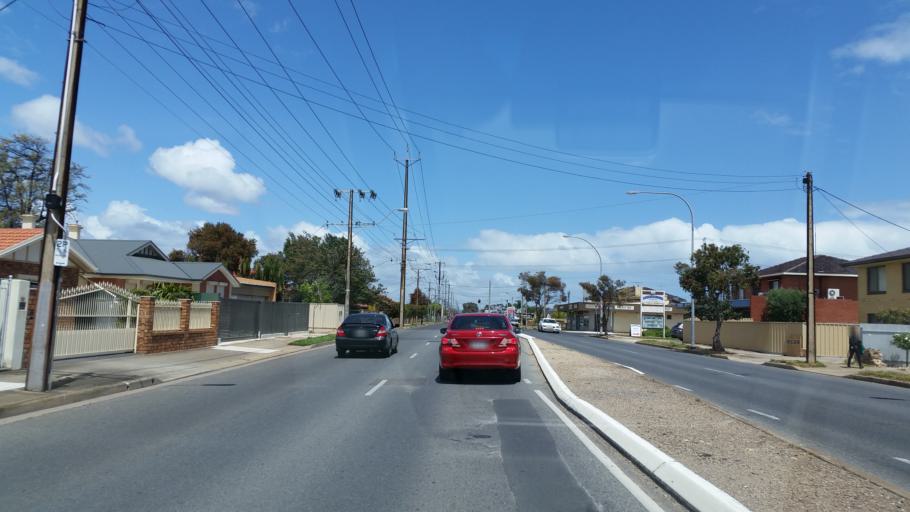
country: AU
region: South Australia
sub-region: Charles Sturt
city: Woodville West
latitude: -34.8886
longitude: 138.5315
